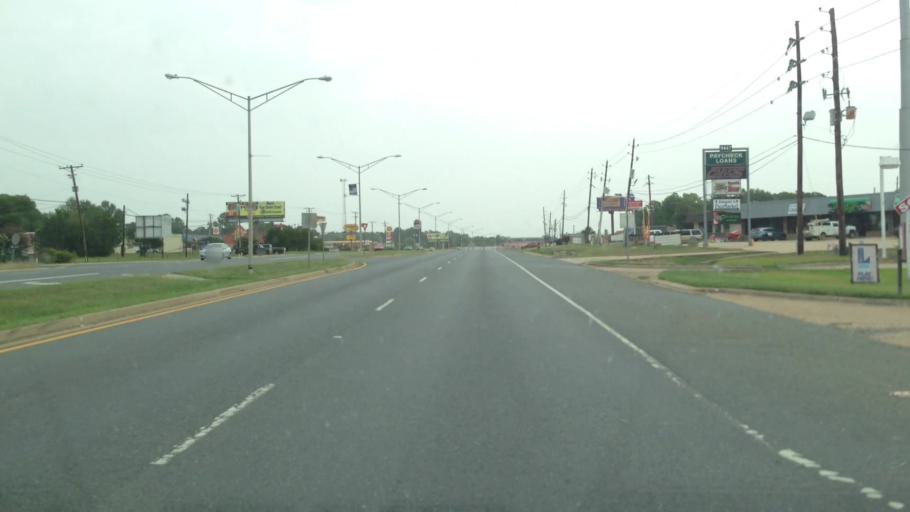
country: US
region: Louisiana
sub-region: De Soto Parish
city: Stonewall
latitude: 32.3916
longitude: -93.8133
